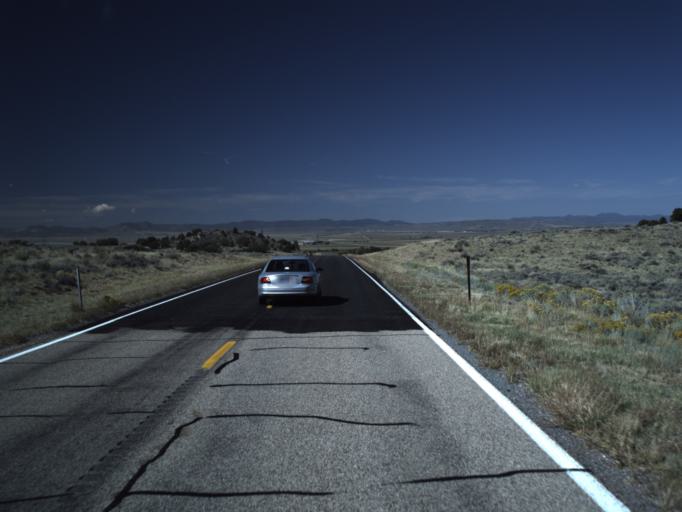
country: US
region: Utah
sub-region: Washington County
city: Enterprise
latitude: 37.6758
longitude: -113.5042
